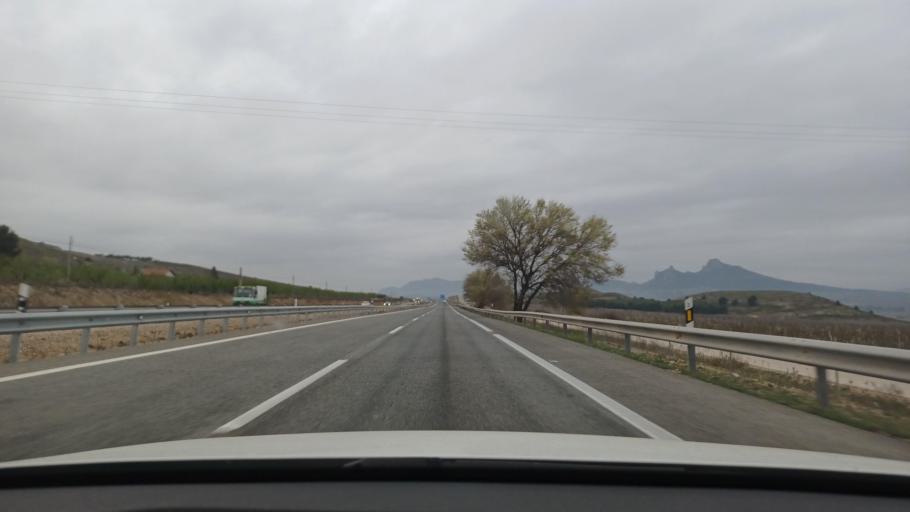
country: ES
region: Valencia
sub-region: Provincia de Alicante
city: Villena
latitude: 38.5893
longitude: -0.8440
